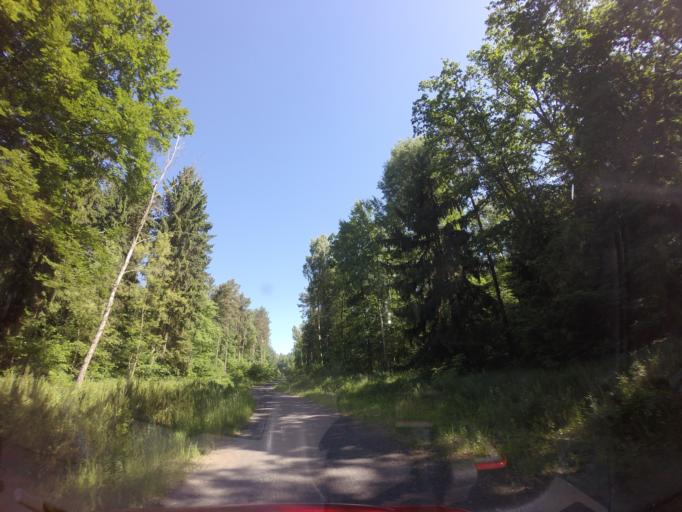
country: PL
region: West Pomeranian Voivodeship
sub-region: Powiat choszczenski
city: Choszczno
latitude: 53.1902
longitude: 15.3635
